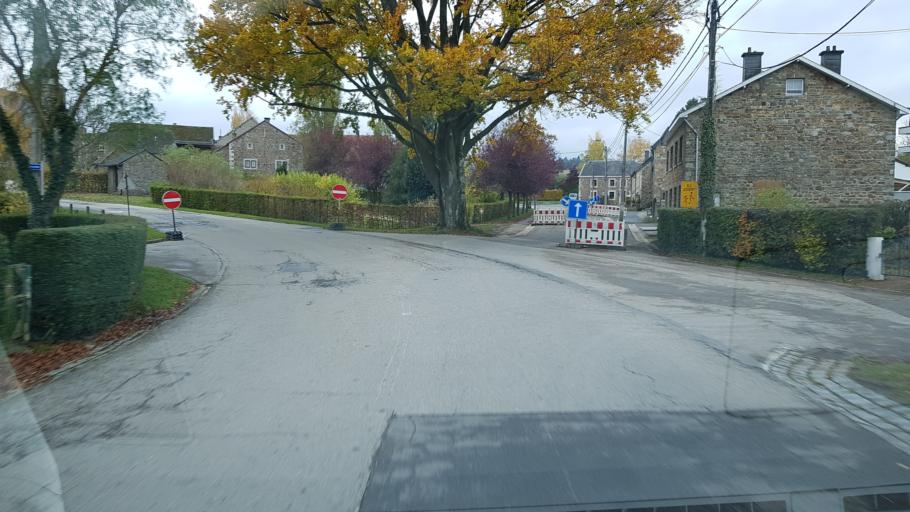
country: BE
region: Wallonia
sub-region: Province de Liege
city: Theux
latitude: 50.4908
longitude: 5.7916
